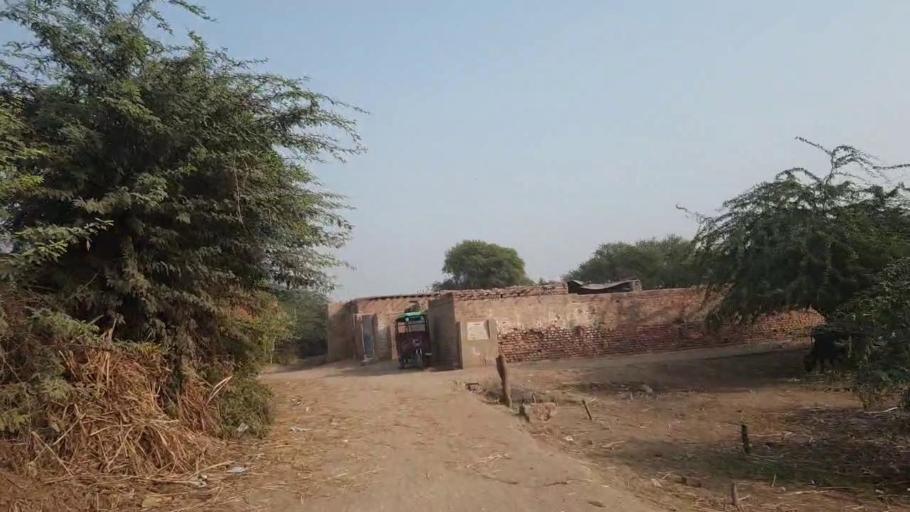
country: PK
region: Sindh
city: Tando Muhammad Khan
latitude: 25.1433
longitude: 68.6141
